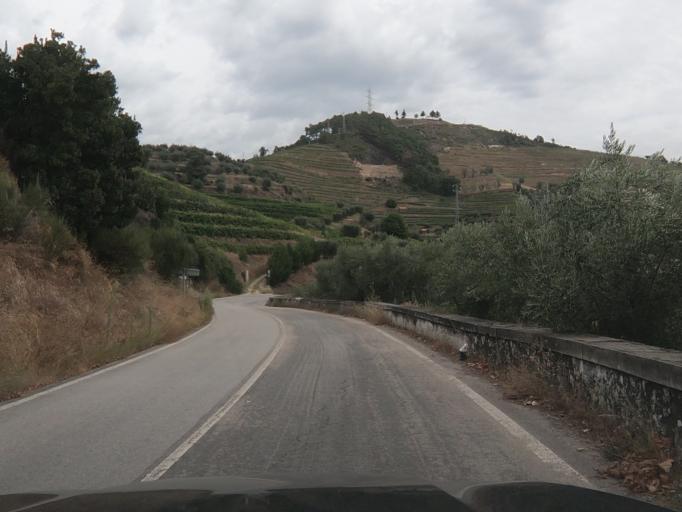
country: PT
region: Vila Real
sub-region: Santa Marta de Penaguiao
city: Santa Marta de Penaguiao
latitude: 41.2400
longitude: -7.7712
